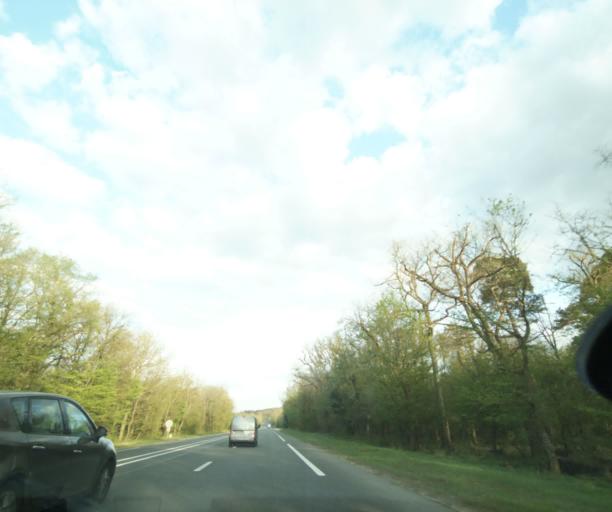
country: FR
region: Ile-de-France
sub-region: Departement de Seine-et-Marne
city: Barbizon
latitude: 48.4445
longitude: 2.6405
